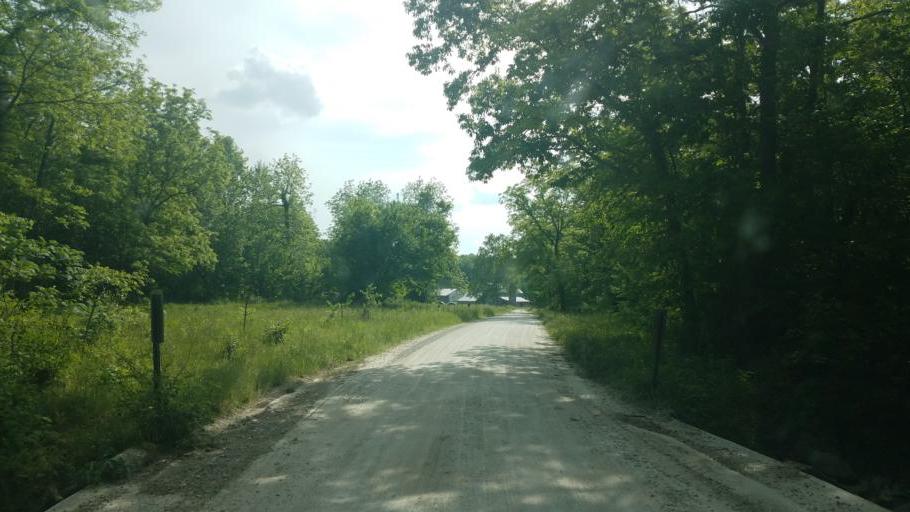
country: US
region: Missouri
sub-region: Cooper County
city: Boonville
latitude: 38.8488
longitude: -92.6512
